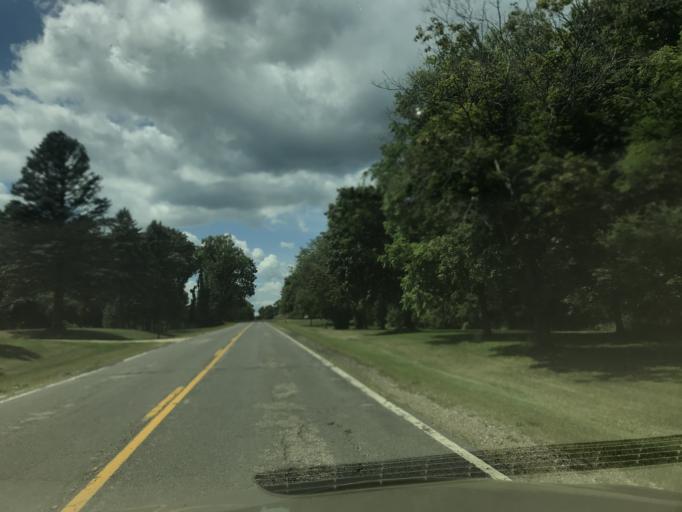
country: US
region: Michigan
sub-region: Ingham County
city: Leslie
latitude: 42.4510
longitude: -84.5440
